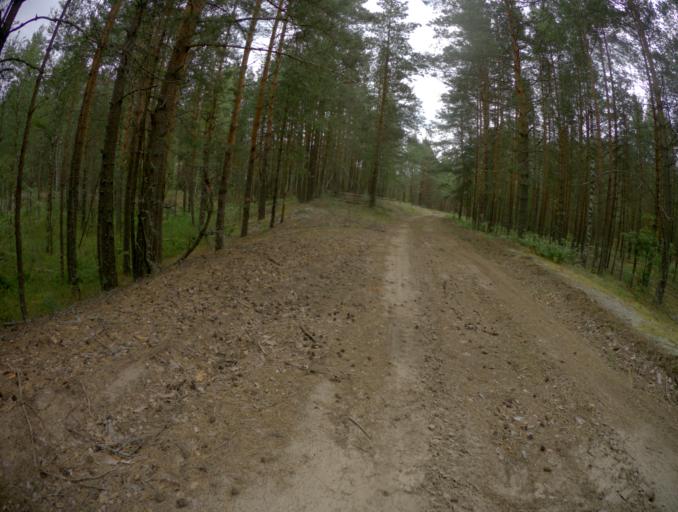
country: RU
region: Nizjnij Novgorod
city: Frolishchi
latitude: 56.3179
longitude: 42.6837
